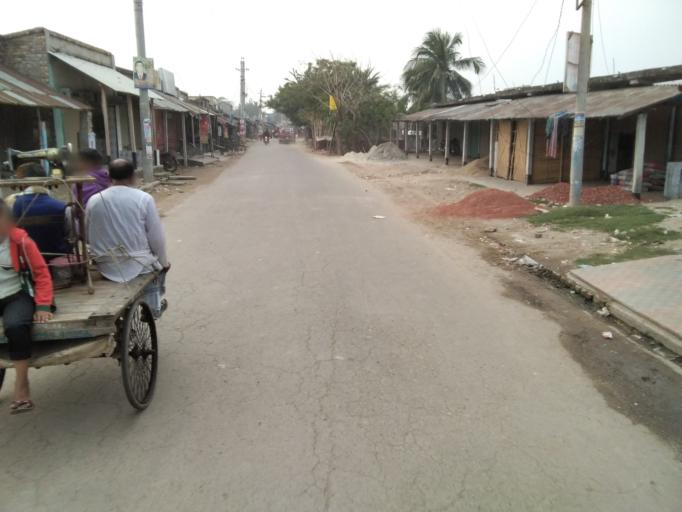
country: BD
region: Khulna
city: Satkhira
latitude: 22.5872
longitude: 89.0640
